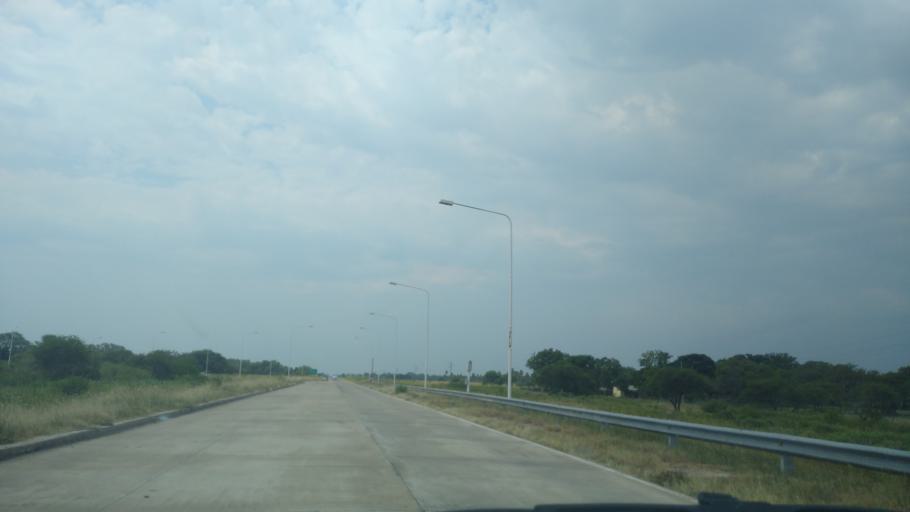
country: AR
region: Chaco
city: Margarita Belen
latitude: -27.0874
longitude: -58.9569
